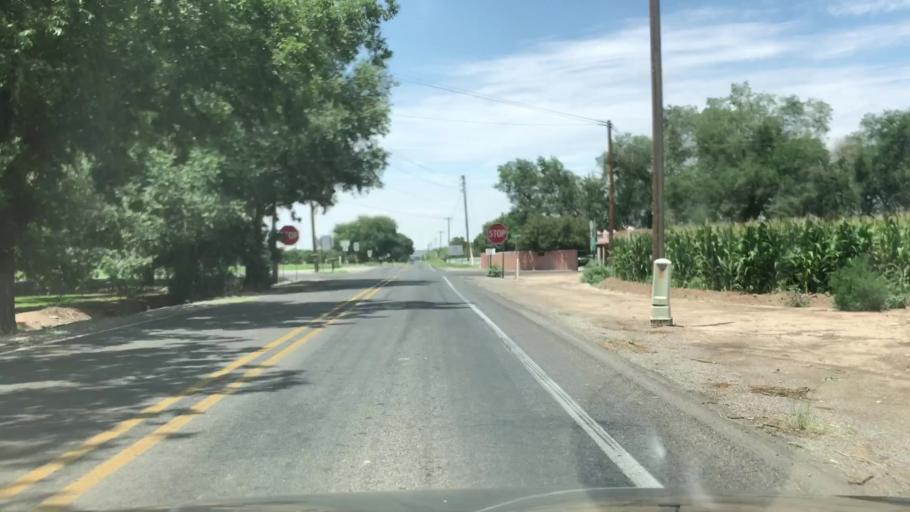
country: US
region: New Mexico
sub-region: Dona Ana County
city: Vado
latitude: 32.1117
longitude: -106.6829
